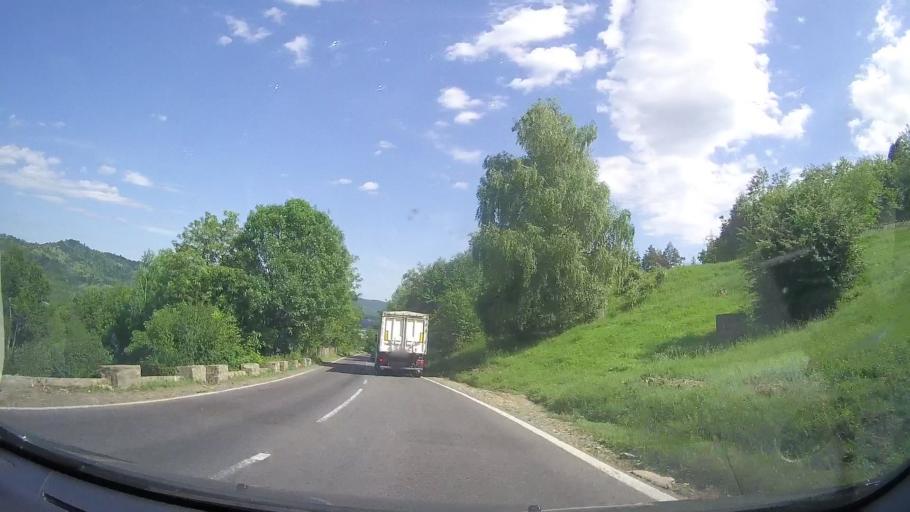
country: RO
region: Prahova
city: Maneciu
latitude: 45.3285
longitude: 25.9784
